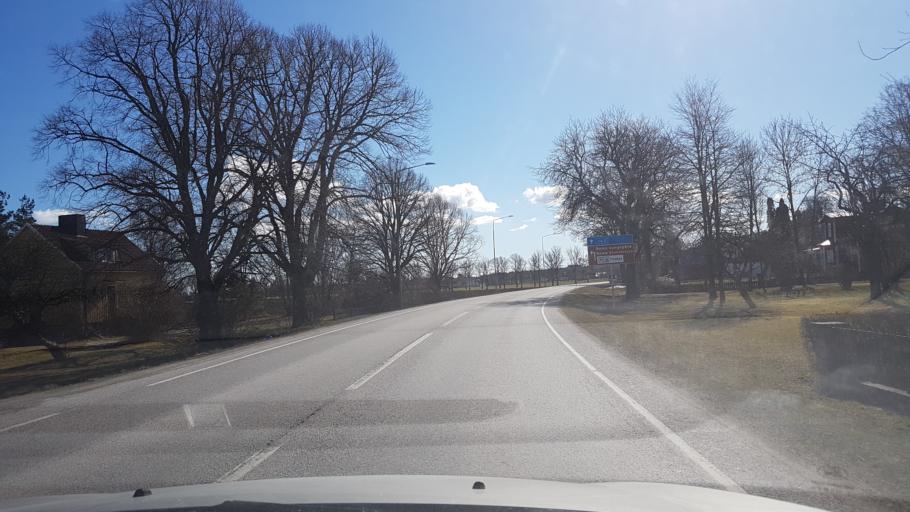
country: SE
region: Gotland
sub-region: Gotland
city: Visby
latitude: 57.5171
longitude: 18.4442
